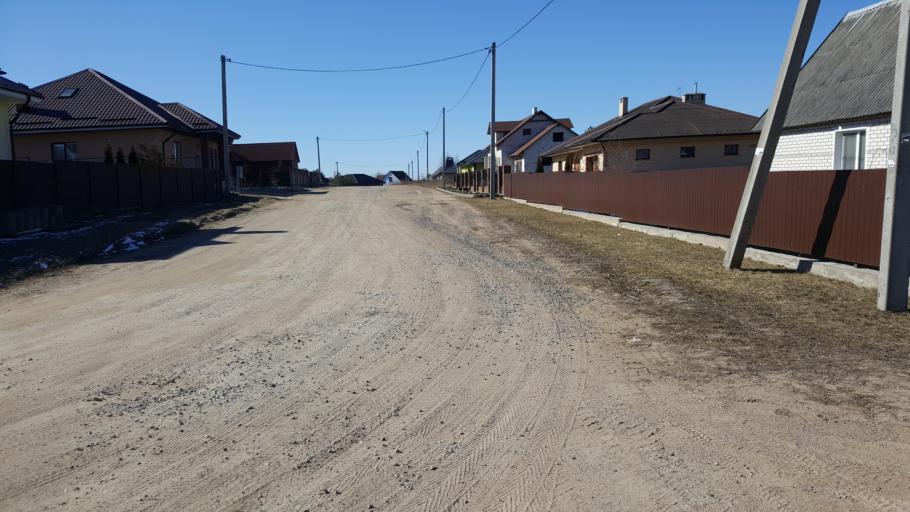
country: BY
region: Brest
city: Kamyanyets
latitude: 52.4052
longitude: 23.8427
